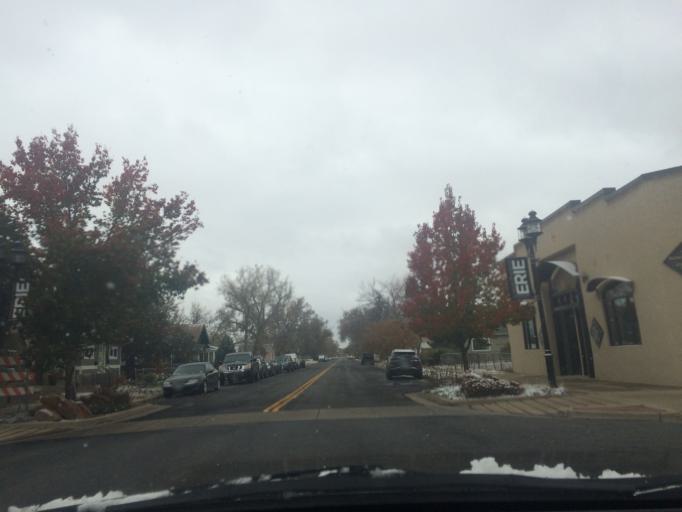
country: US
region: Colorado
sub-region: Boulder County
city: Erie
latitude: 40.0491
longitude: -105.0474
